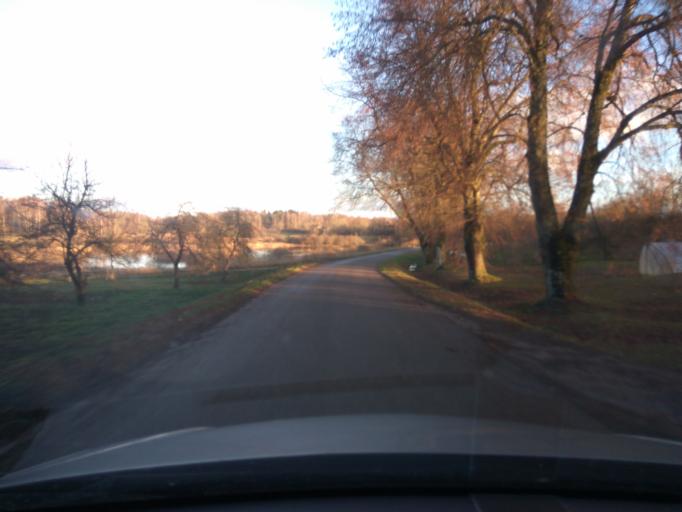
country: LV
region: Aizpute
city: Aizpute
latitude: 56.8360
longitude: 21.7739
